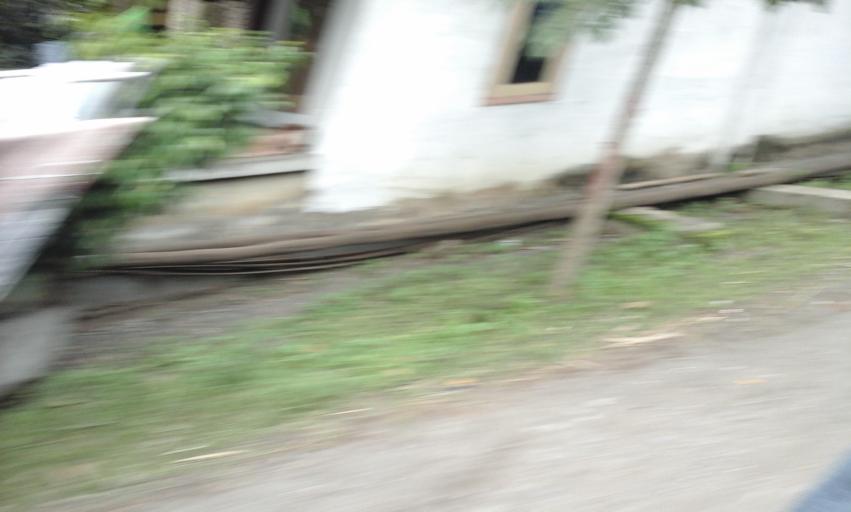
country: ID
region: East Java
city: Petung
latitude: -8.2036
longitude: 113.5738
